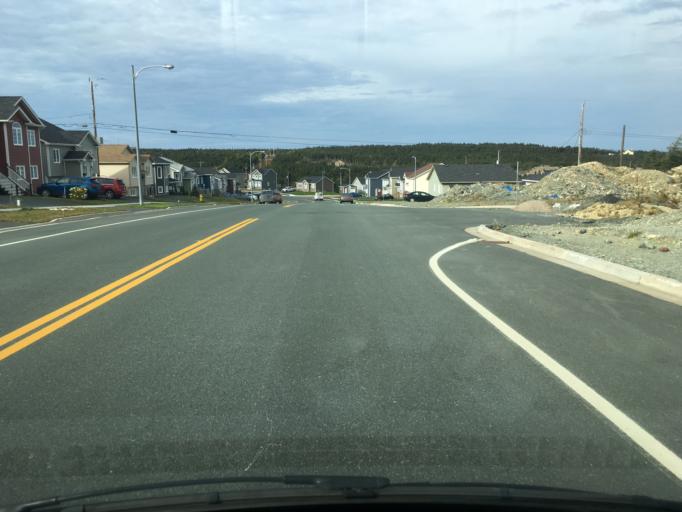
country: CA
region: Newfoundland and Labrador
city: Mount Pearl
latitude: 47.5531
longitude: -52.7907
